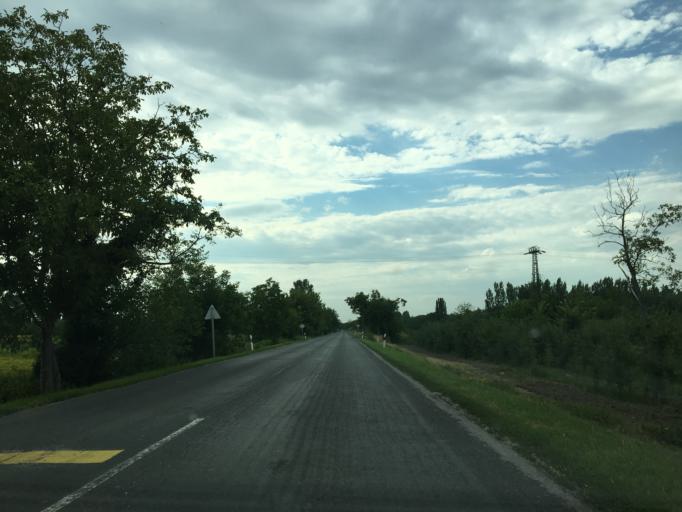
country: HU
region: Bacs-Kiskun
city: Dusnok
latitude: 46.3853
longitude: 18.9558
